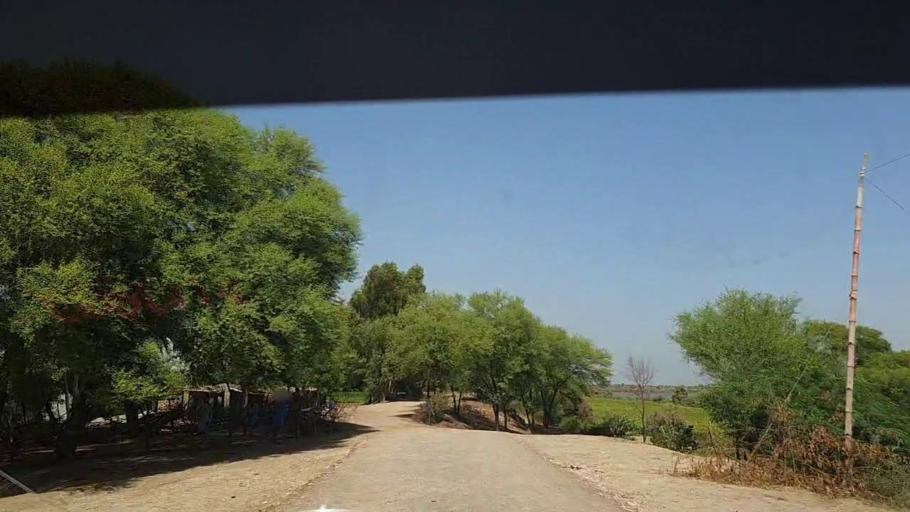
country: PK
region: Sindh
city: Ghauspur
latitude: 28.1693
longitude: 69.1425
